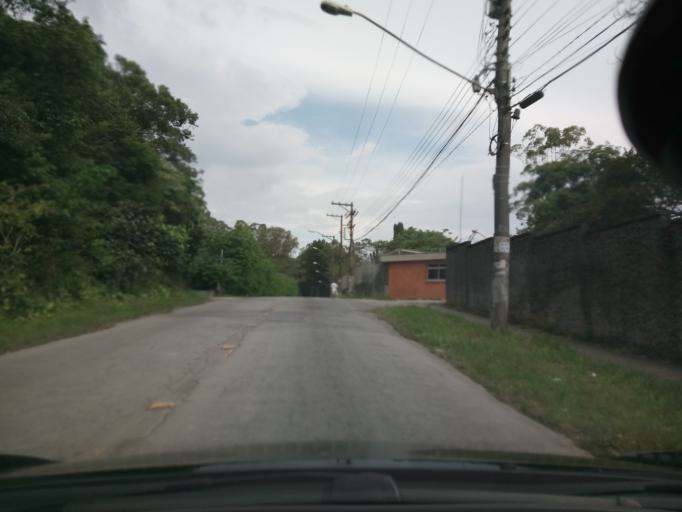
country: BR
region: Sao Paulo
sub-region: Sao Bernardo Do Campo
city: Sao Bernardo do Campo
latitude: -23.7466
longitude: -46.5953
